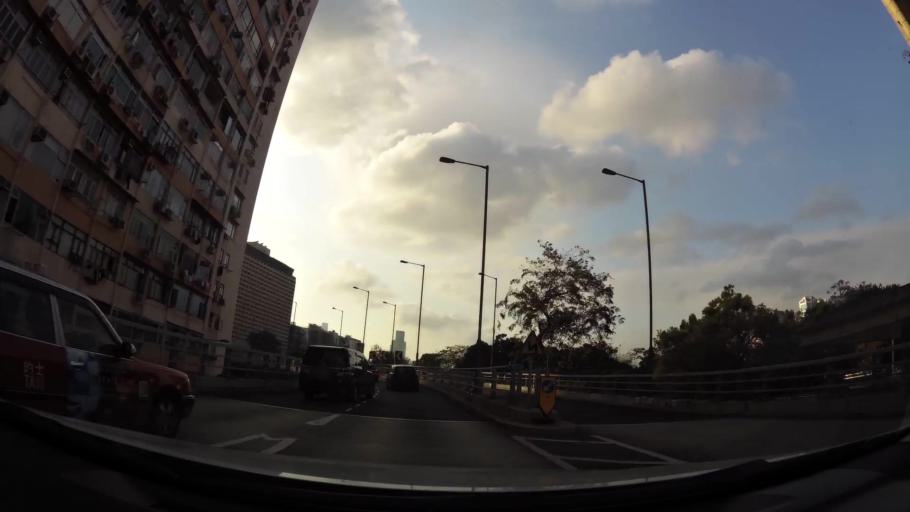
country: HK
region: Wanchai
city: Wan Chai
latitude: 22.2798
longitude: 114.1890
